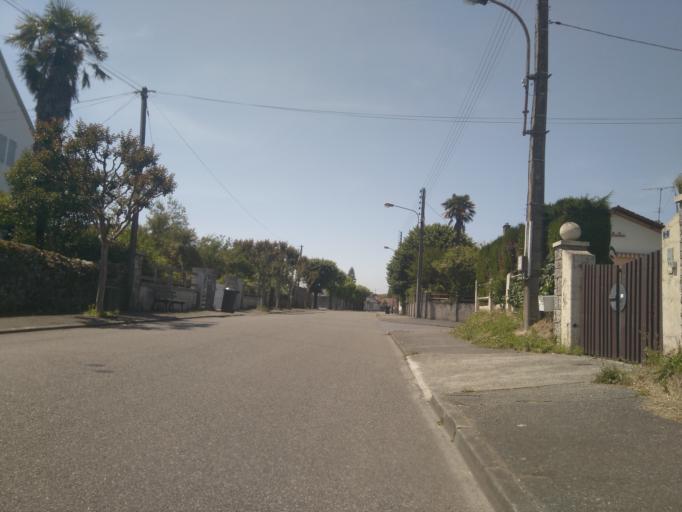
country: FR
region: Aquitaine
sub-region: Departement des Pyrenees-Atlantiques
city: Orthez
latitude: 43.4895
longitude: -0.7795
